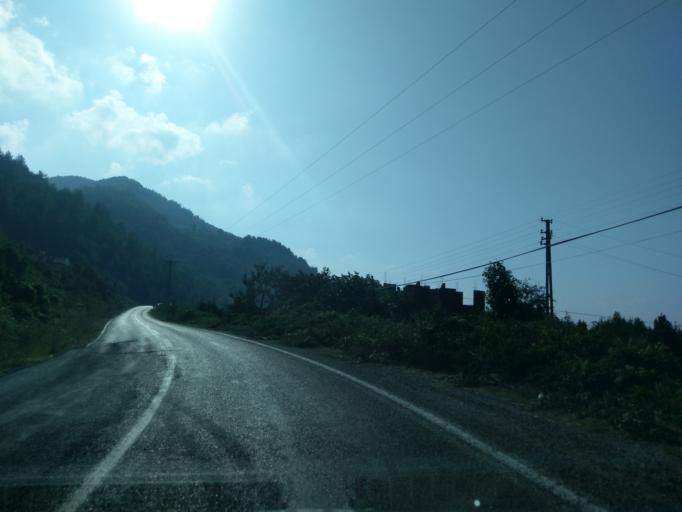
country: TR
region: Sinop
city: Ayancik
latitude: 41.9417
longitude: 34.6529
